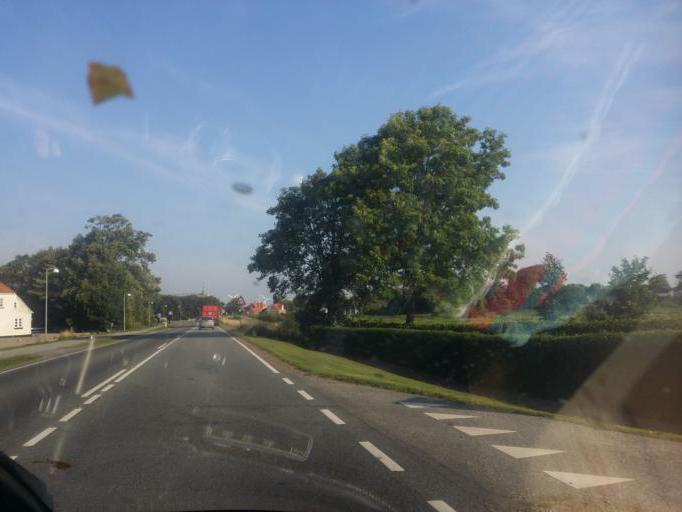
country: DK
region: South Denmark
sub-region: Tonder Kommune
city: Sherrebek
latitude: 55.1907
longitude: 8.7295
